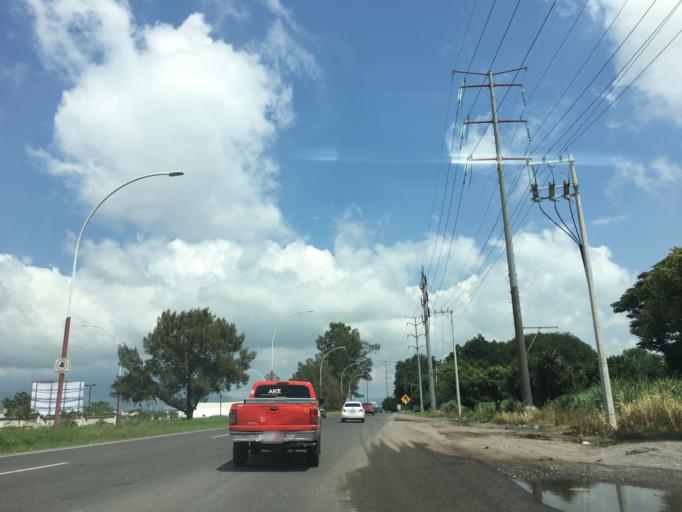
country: MX
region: Nayarit
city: Xalisco
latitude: 21.4698
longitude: -104.8874
